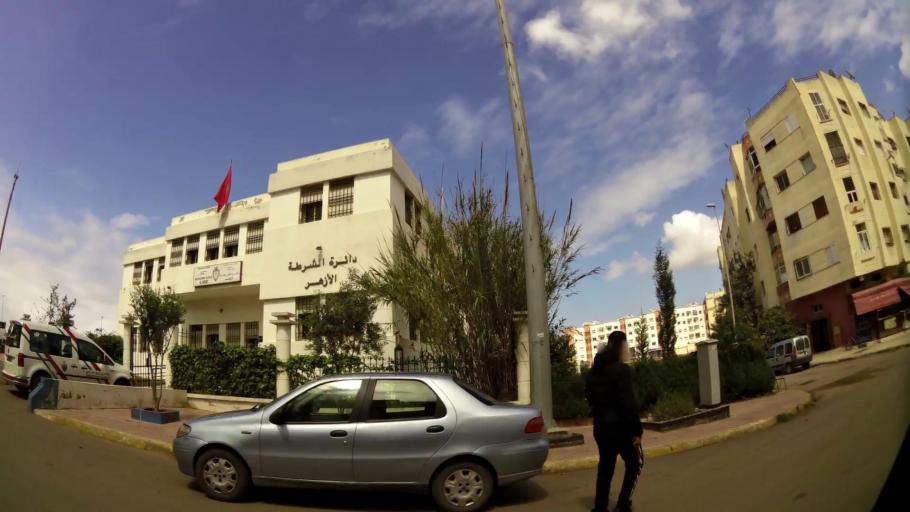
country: MA
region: Grand Casablanca
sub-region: Mediouna
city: Tit Mellil
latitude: 33.6046
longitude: -7.4838
